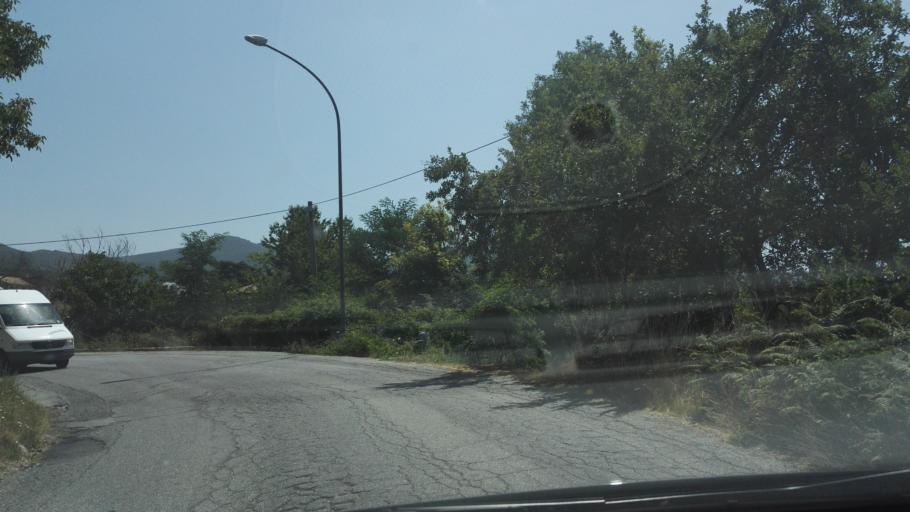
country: IT
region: Calabria
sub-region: Provincia di Vibo-Valentia
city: Mongiana
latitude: 38.5145
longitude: 16.3159
